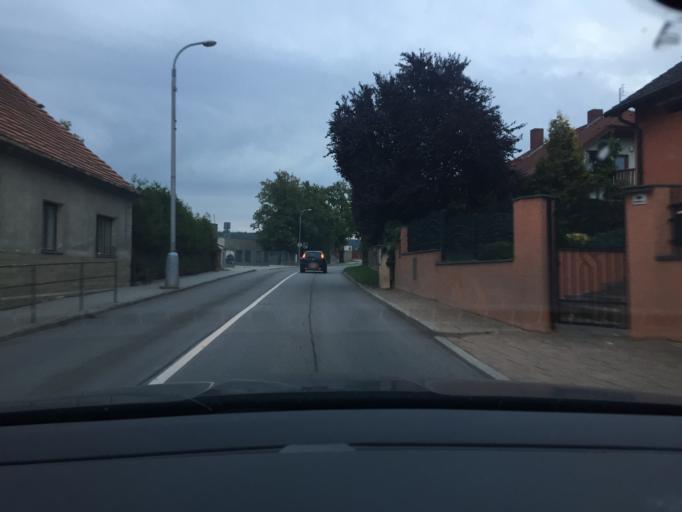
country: CZ
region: Jihocesky
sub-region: Okres Ceske Budejovice
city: Hluboka nad Vltavou
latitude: 49.0543
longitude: 14.4482
